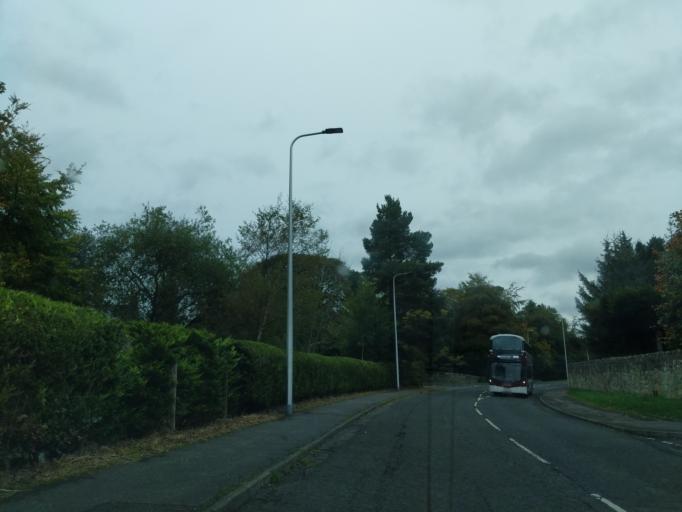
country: GB
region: Scotland
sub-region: Edinburgh
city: Balerno
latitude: 55.8794
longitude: -3.3499
